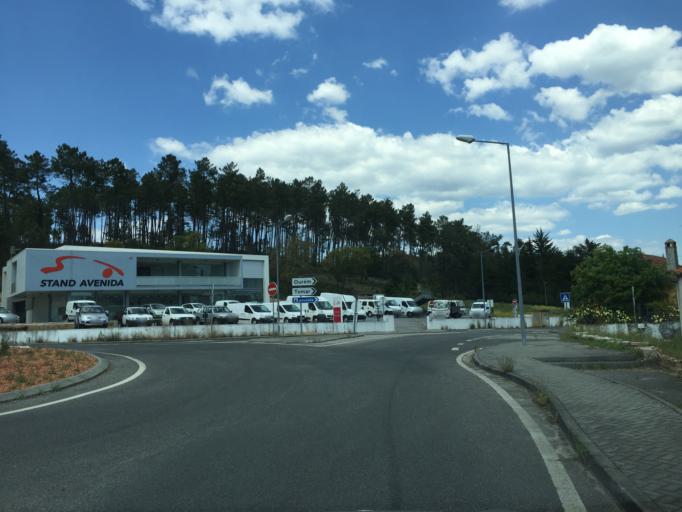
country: PT
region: Santarem
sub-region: Ourem
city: Ourem
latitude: 39.6530
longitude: -8.6100
